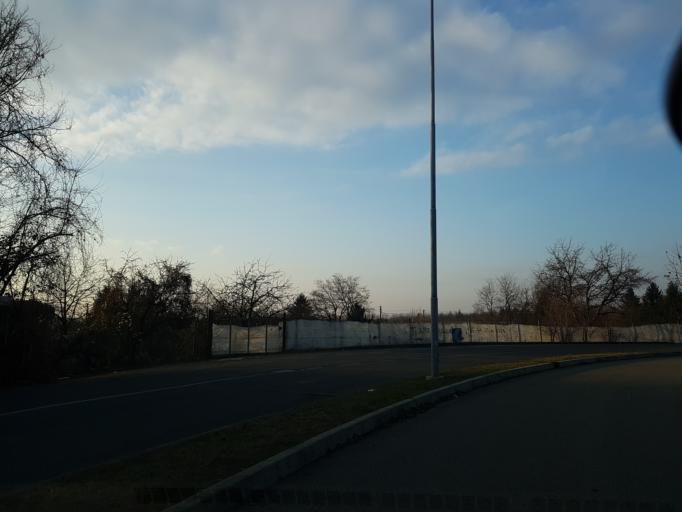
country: IT
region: Piedmont
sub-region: Provincia di Alessandria
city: Pozzolo Formigaro
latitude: 44.7882
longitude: 8.7806
